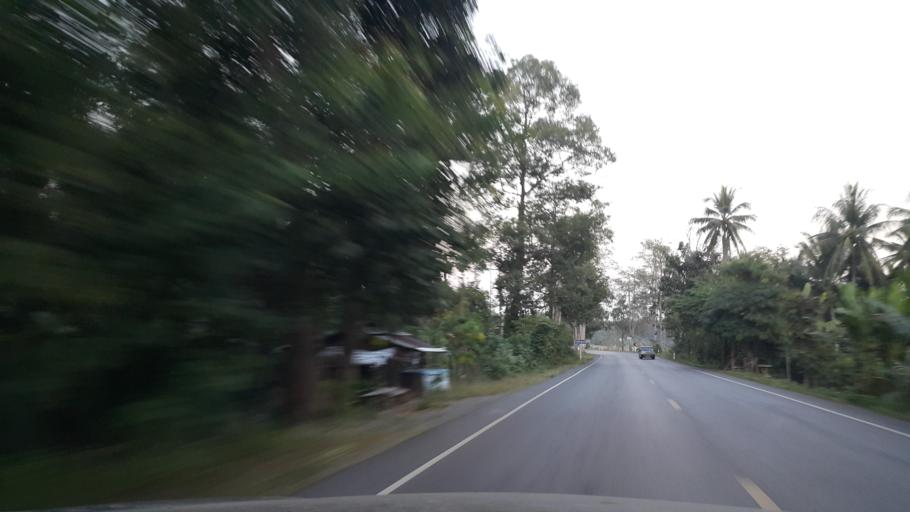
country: TH
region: Phrae
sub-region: Amphoe Wang Chin
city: Wang Chin
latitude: 17.9748
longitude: 99.6336
